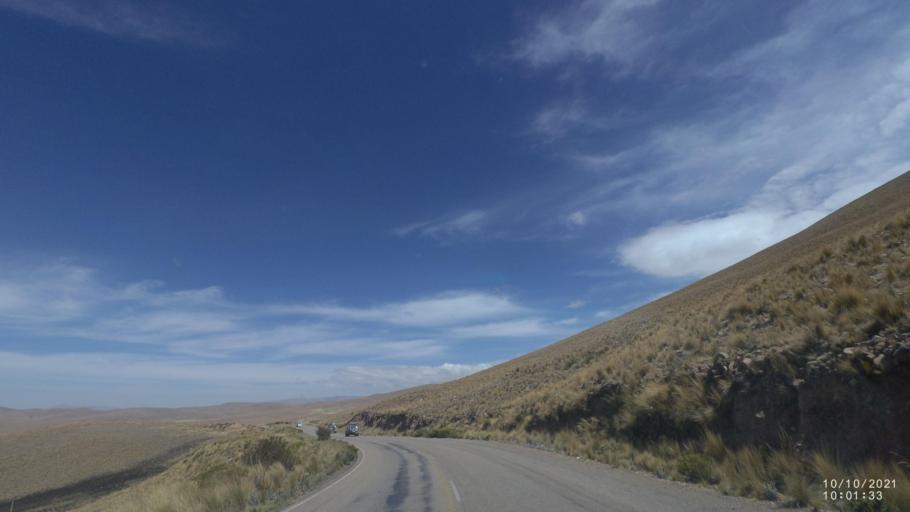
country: BO
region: La Paz
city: Eucaliptus
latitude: -17.3650
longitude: -67.4231
